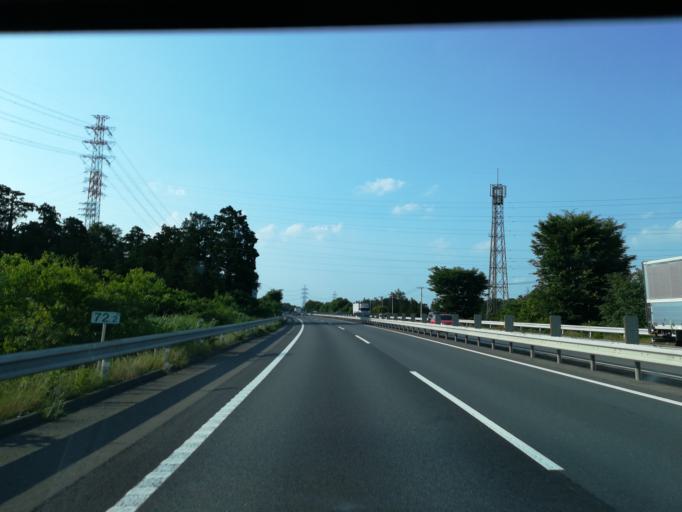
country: JP
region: Saitama
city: Sayama
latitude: 35.8875
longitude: 139.3880
